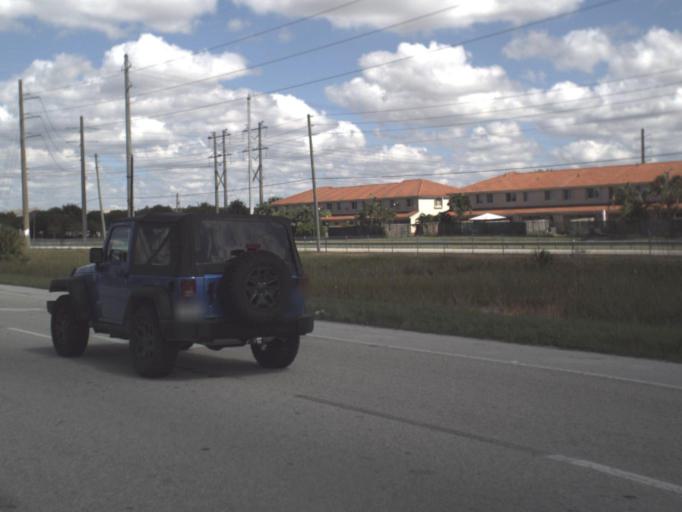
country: US
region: Florida
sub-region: Miami-Dade County
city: Doral
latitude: 25.8166
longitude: -80.3864
